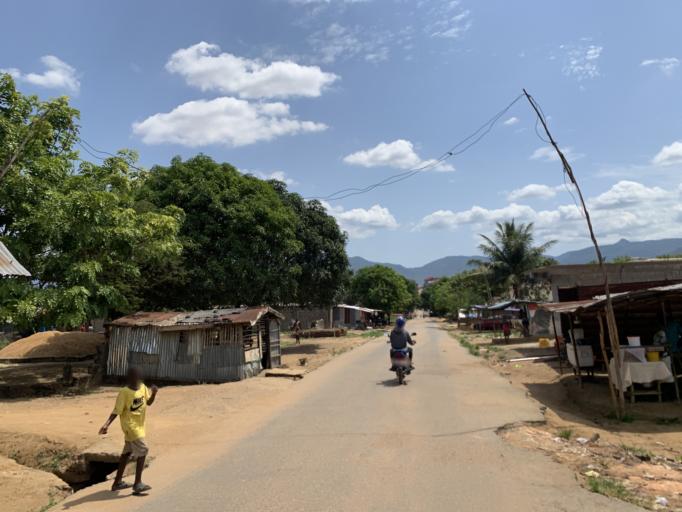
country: SL
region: Western Area
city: Waterloo
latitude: 8.3312
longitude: -13.0447
